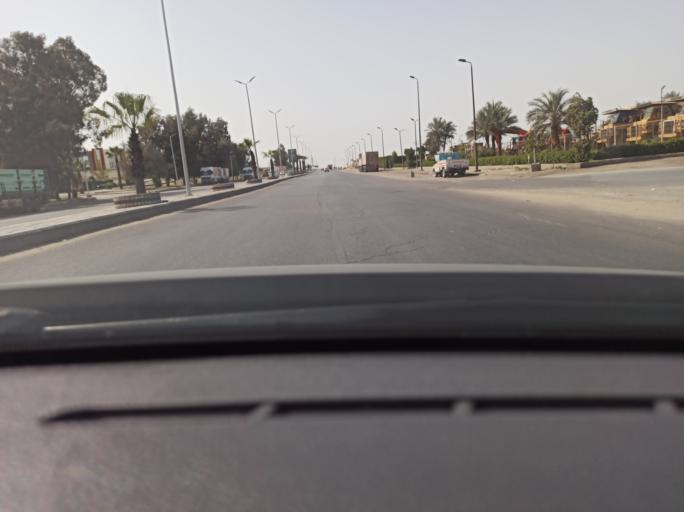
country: EG
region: Muhafazat al Qahirah
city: Halwan
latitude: 29.8228
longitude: 31.3531
